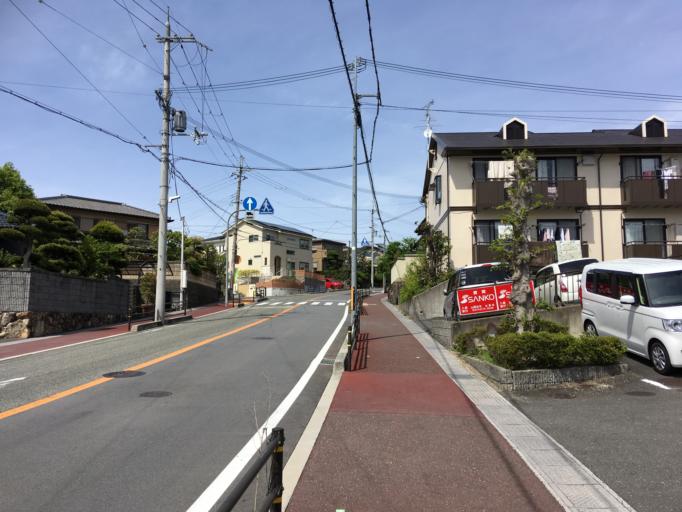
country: JP
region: Nara
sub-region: Ikoma-shi
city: Ikoma
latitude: 34.7032
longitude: 135.6989
